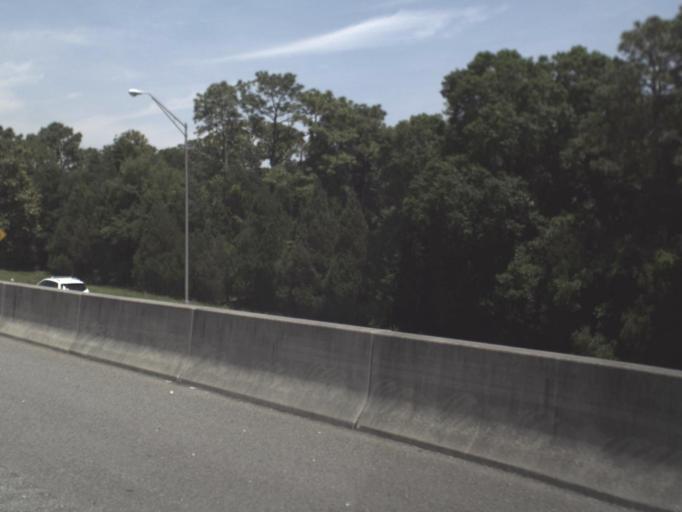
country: US
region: Florida
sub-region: Duval County
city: Jacksonville
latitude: 30.3257
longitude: -81.5279
